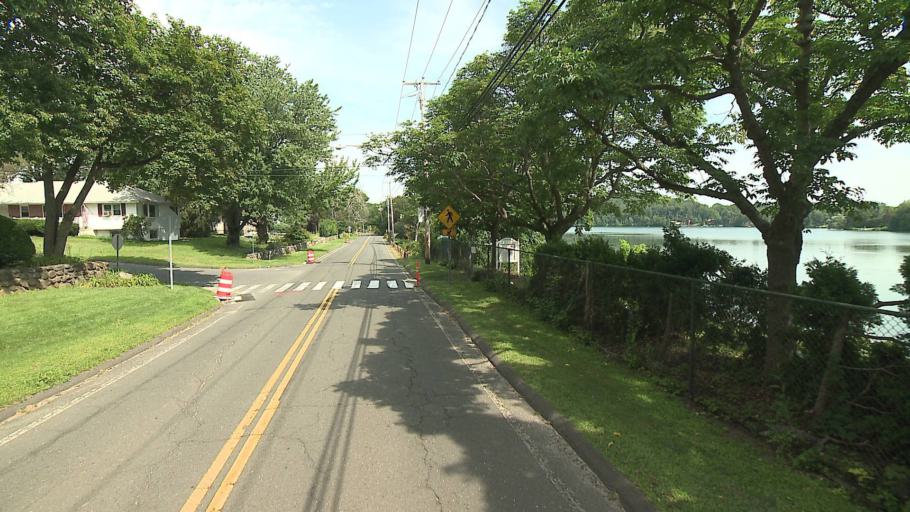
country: US
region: New York
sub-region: Putnam County
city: Putnam Lake
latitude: 41.4599
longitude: -73.5251
